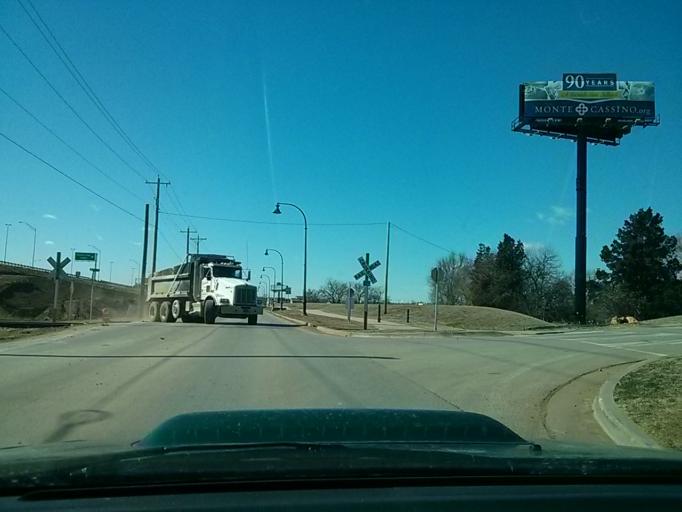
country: US
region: Oklahoma
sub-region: Tulsa County
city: Jenks
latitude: 36.0174
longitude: -95.9678
